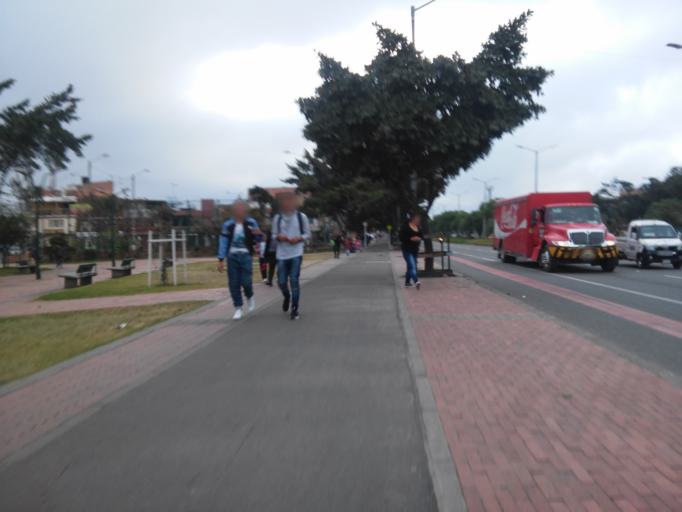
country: CO
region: Cundinamarca
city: Soacha
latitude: 4.6142
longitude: -74.1652
